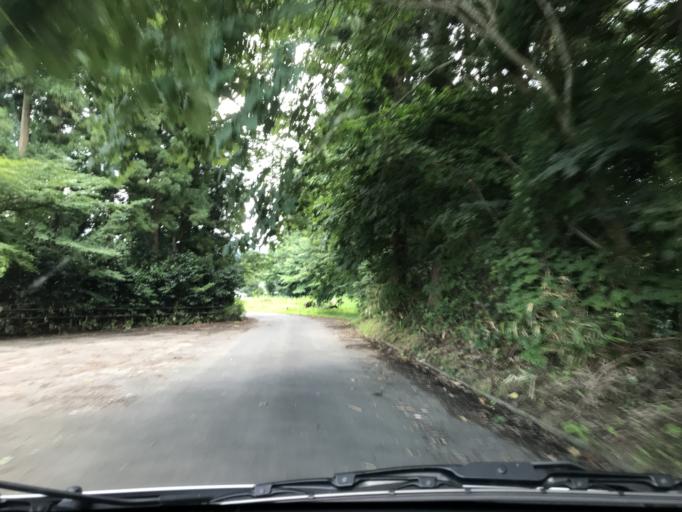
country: JP
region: Iwate
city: Ichinoseki
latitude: 39.0101
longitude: 141.0942
